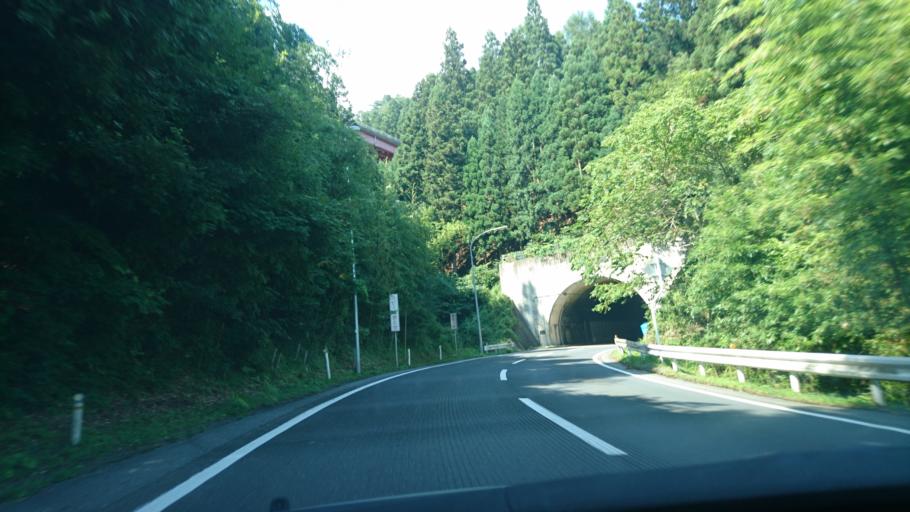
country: JP
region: Iwate
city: Ofunato
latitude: 39.0092
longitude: 141.4846
